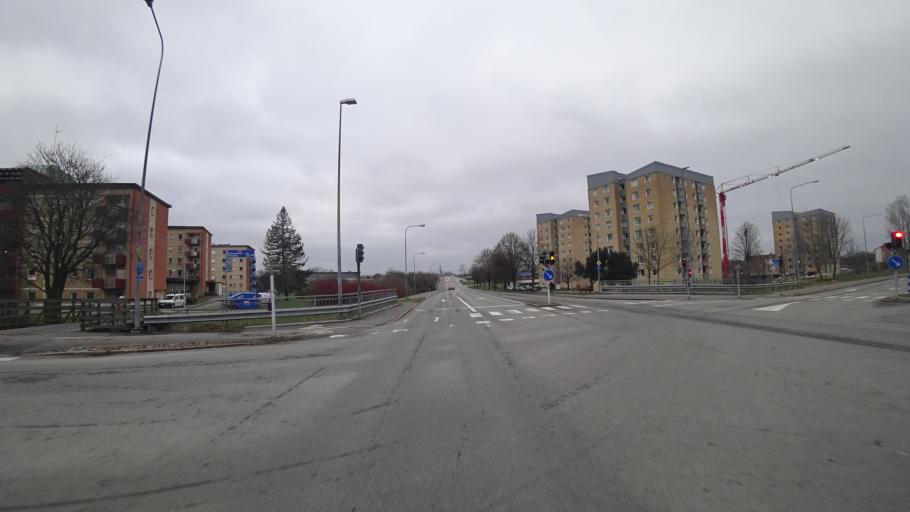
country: SE
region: Skane
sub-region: Kristianstads Kommun
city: Kristianstad
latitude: 56.0393
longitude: 14.1619
